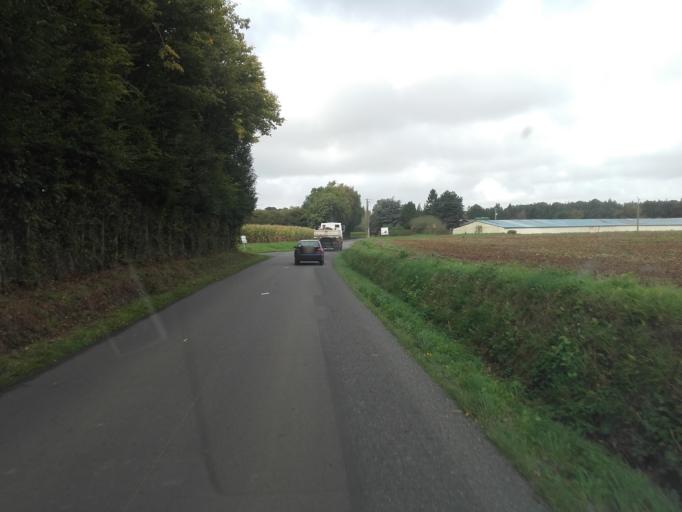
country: FR
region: Brittany
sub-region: Departement des Cotes-d'Armor
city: Plelo
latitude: 48.5773
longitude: -2.9496
